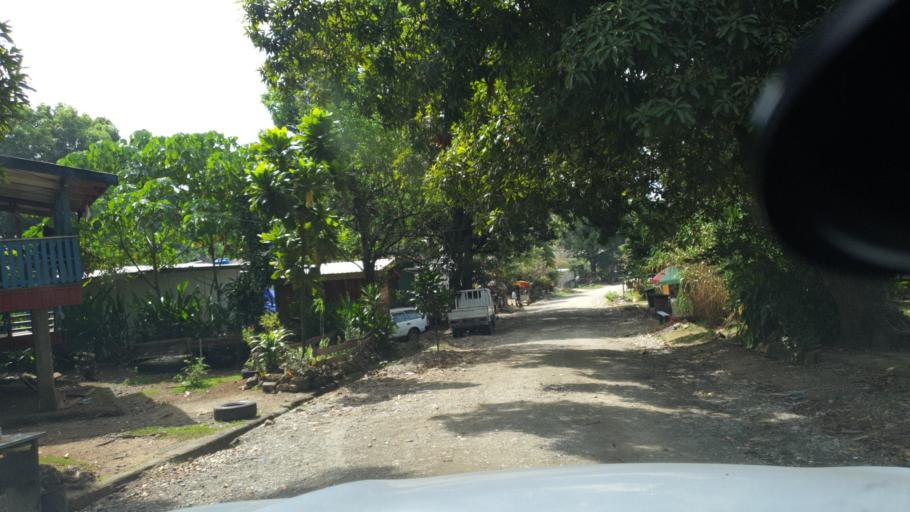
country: SB
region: Guadalcanal
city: Honiara
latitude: -9.4371
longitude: 159.9849
